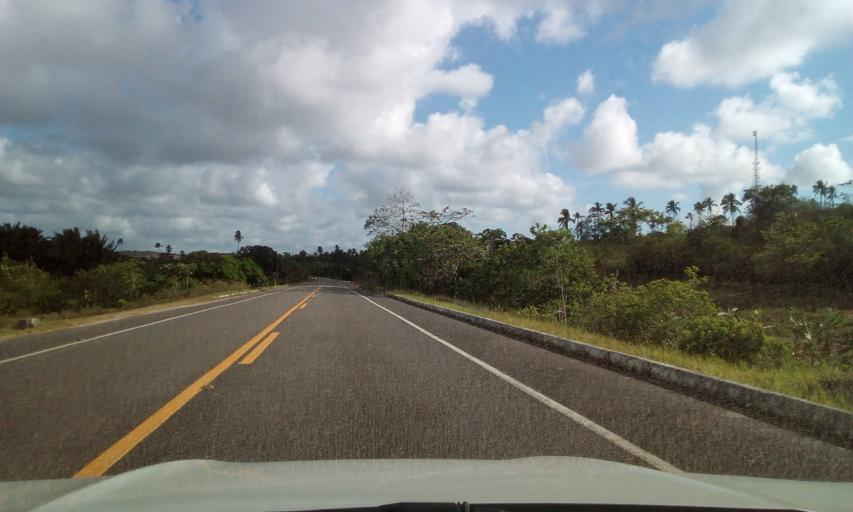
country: BR
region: Bahia
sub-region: Conde
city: Conde
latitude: -11.8024
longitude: -37.6288
